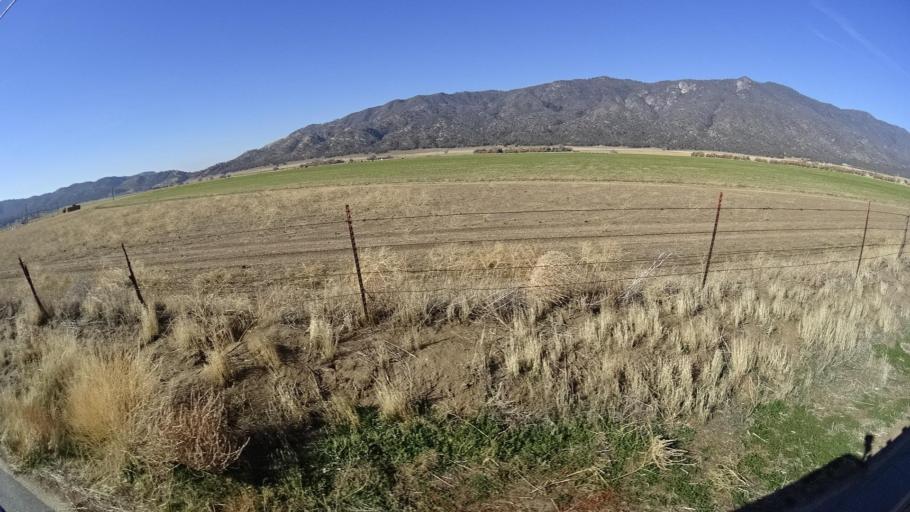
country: US
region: California
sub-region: Kern County
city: Bodfish
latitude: 35.4042
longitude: -118.5230
